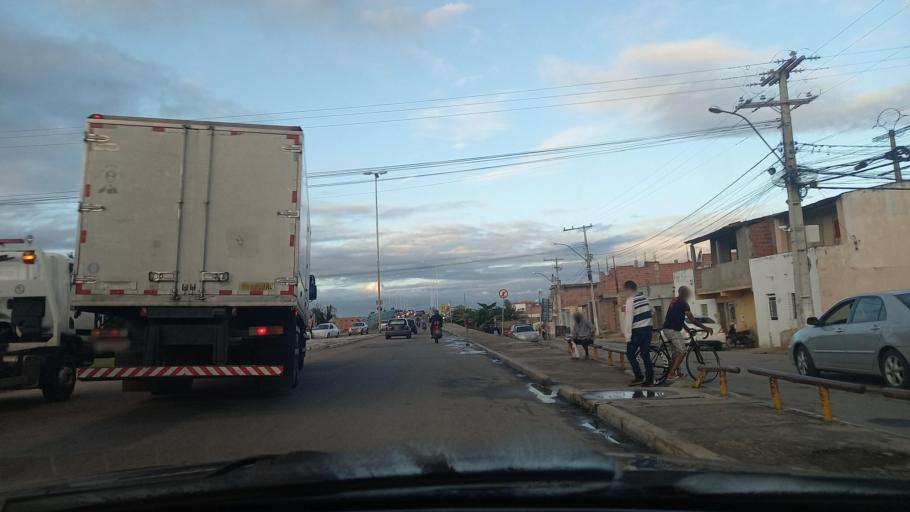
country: BR
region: Bahia
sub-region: Paulo Afonso
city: Paulo Afonso
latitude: -9.4015
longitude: -38.2369
